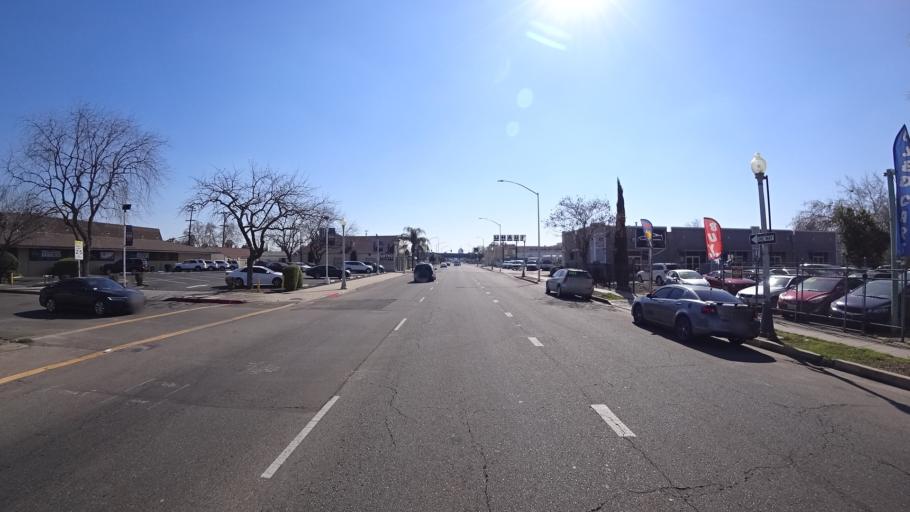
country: US
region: California
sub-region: Fresno County
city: Fresno
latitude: 36.7546
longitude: -119.7906
